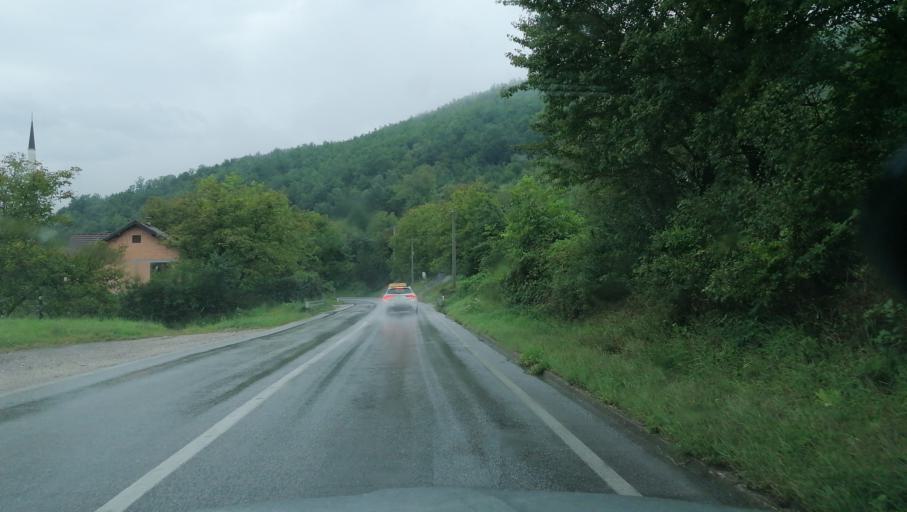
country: BA
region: Federation of Bosnia and Herzegovina
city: Gorazde
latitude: 43.6776
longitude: 19.0363
